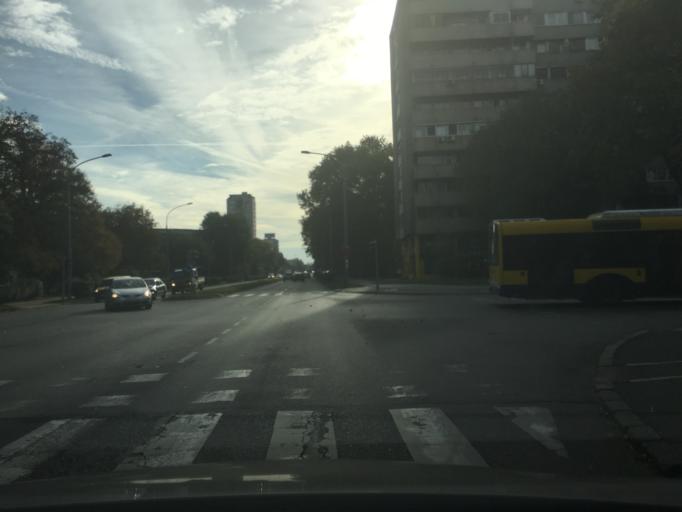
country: RS
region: Central Serbia
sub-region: Belgrade
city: Zemun
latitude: 44.8281
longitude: 20.4039
